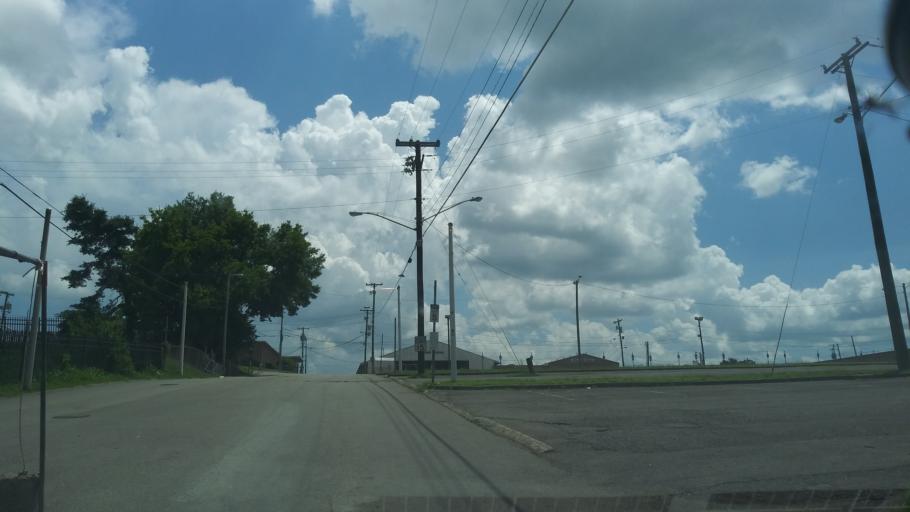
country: US
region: Tennessee
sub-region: Davidson County
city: Nashville
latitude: 36.1322
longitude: -86.7652
